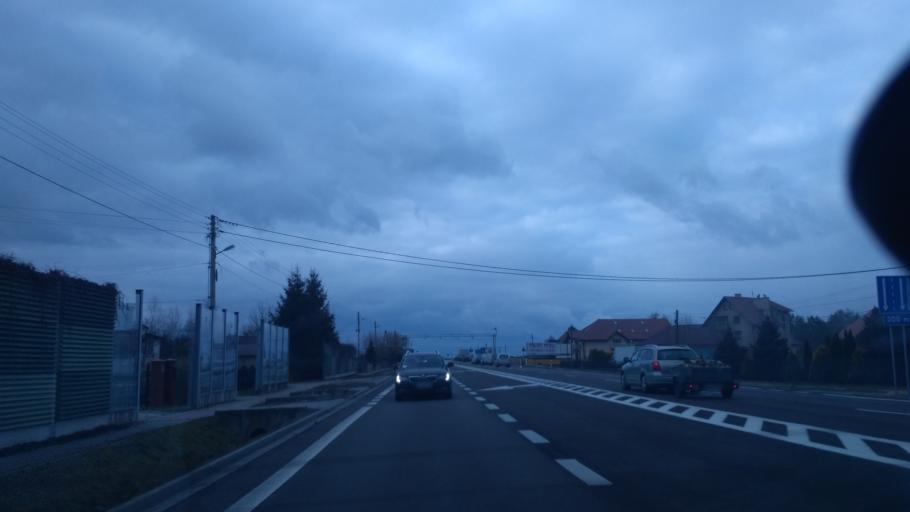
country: PL
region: Subcarpathian Voivodeship
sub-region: Powiat lancucki
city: Kraczkowa
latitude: 50.0439
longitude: 22.1266
